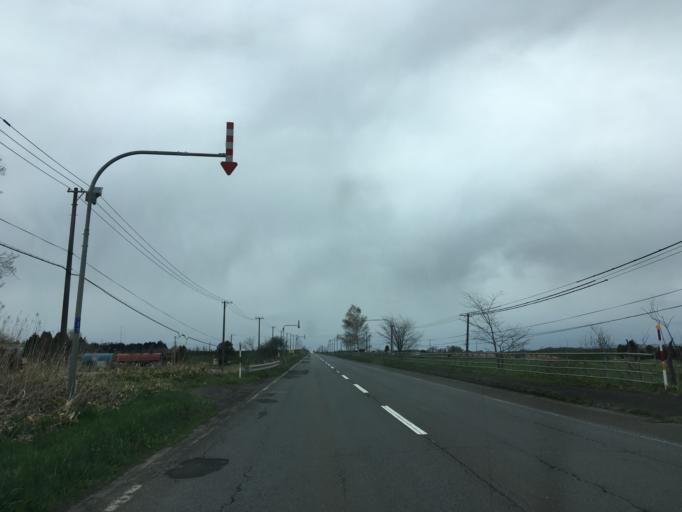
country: JP
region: Hokkaido
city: Chitose
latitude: 42.9194
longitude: 141.8094
